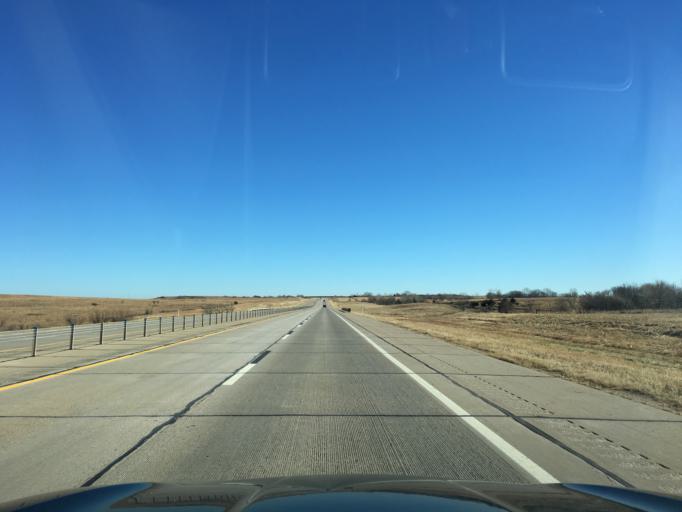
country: US
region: Oklahoma
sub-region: Noble County
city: Perry
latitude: 36.3937
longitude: -97.2077
